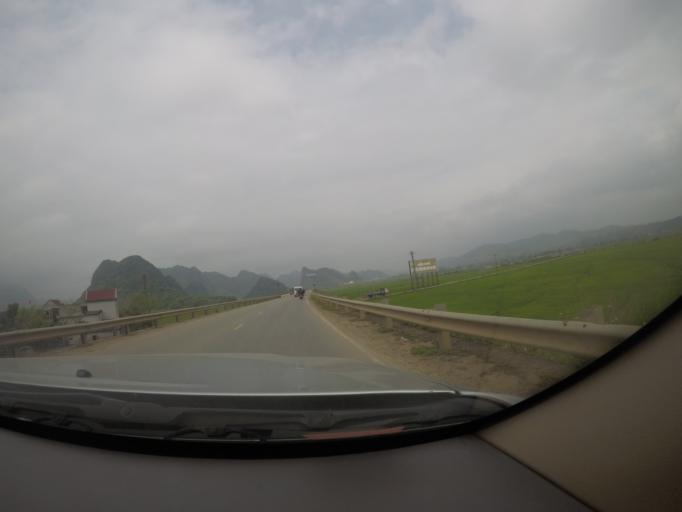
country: VN
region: Quang Binh
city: Ba Don
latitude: 17.6066
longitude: 106.3303
